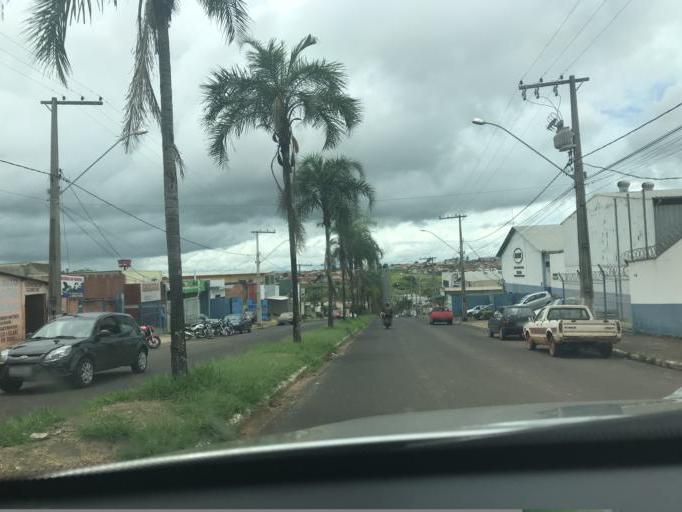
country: BR
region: Minas Gerais
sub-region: Araxa
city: Araxa
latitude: -19.5804
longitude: -46.9350
